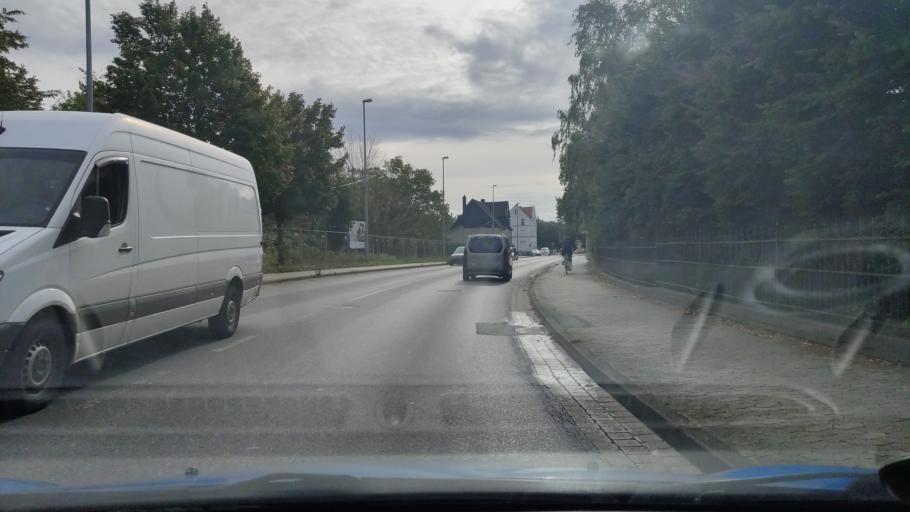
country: DE
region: Lower Saxony
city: Langenhagen
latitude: 52.4259
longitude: 9.7083
